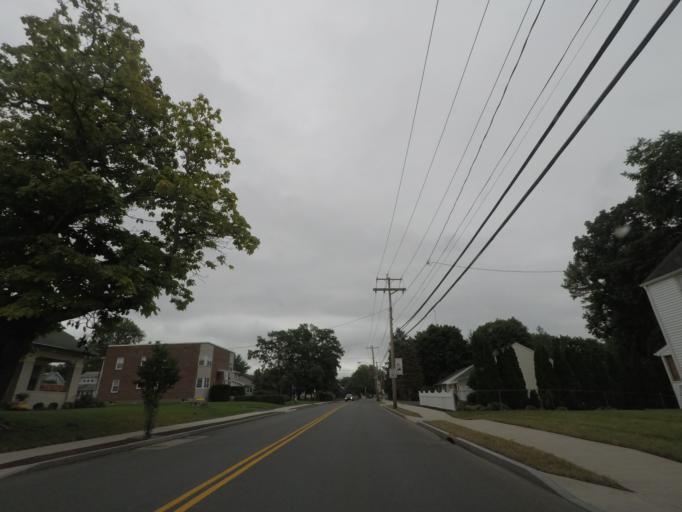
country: US
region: New York
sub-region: Rensselaer County
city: Rensselaer
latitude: 42.6578
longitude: -73.7136
